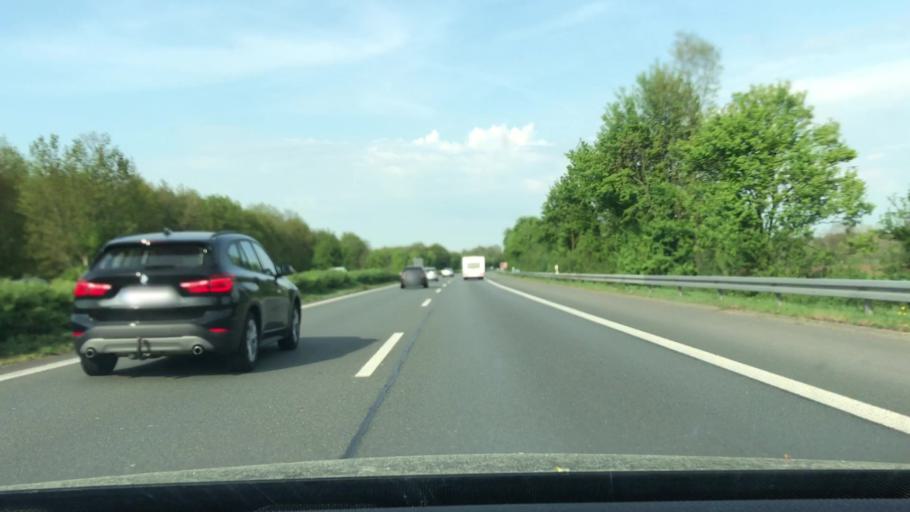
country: DE
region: North Rhine-Westphalia
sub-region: Regierungsbezirk Munster
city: Haltern
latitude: 51.8130
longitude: 7.2019
